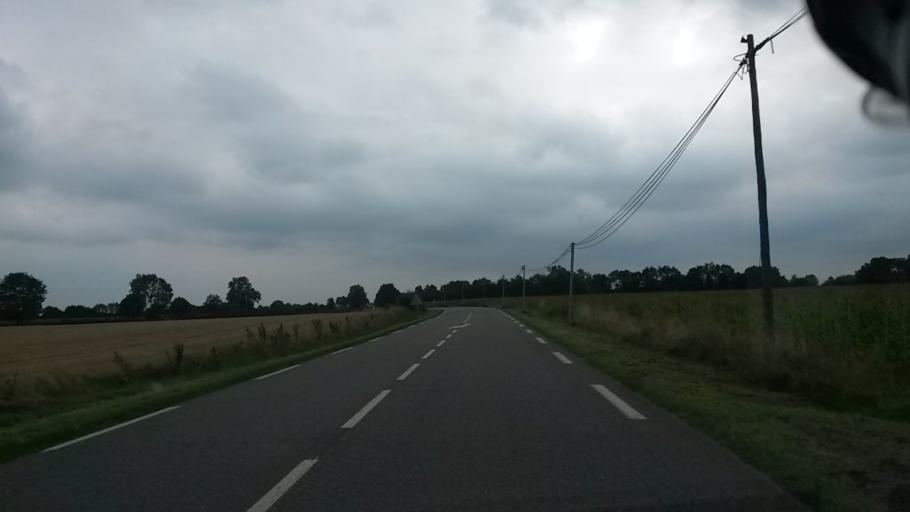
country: FR
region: Haute-Normandie
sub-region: Departement de la Seine-Maritime
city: Gaillefontaine
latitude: 49.6984
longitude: 1.6442
